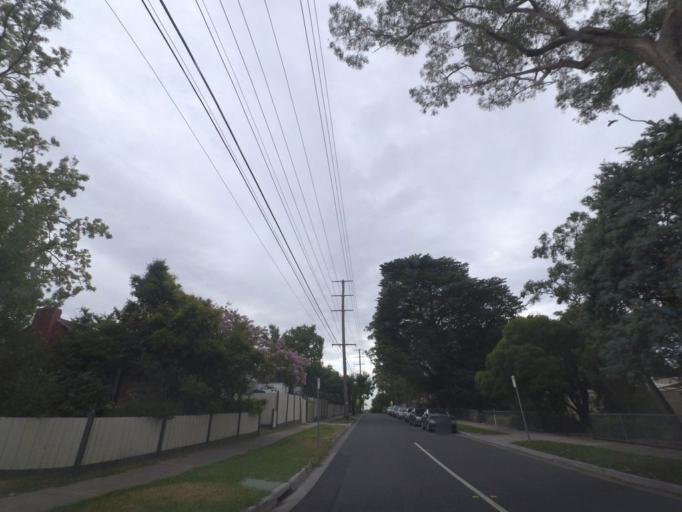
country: AU
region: Victoria
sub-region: Maroondah
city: Ringwood East
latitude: -37.8195
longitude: 145.2310
